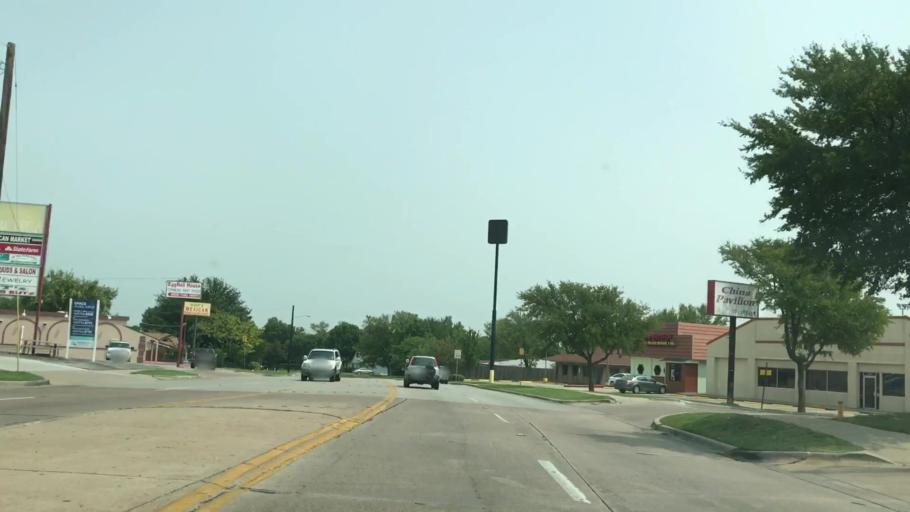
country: US
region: Texas
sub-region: Dallas County
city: Irving
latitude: 32.8474
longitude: -96.9918
